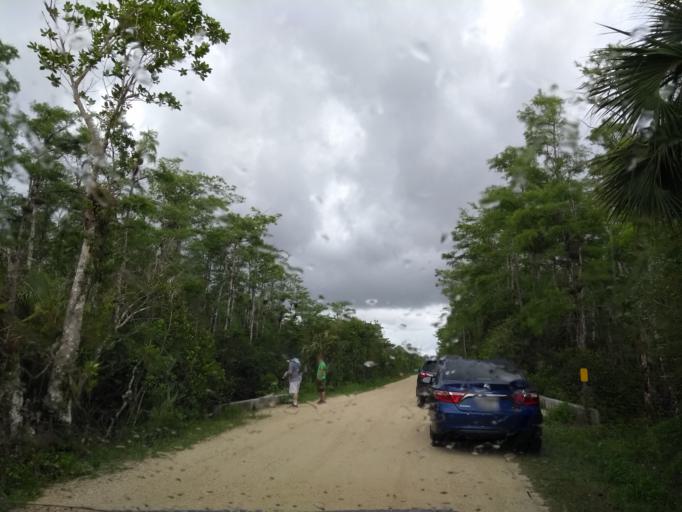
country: US
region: Florida
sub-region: Miami-Dade County
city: The Hammocks
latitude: 25.7476
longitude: -80.9569
